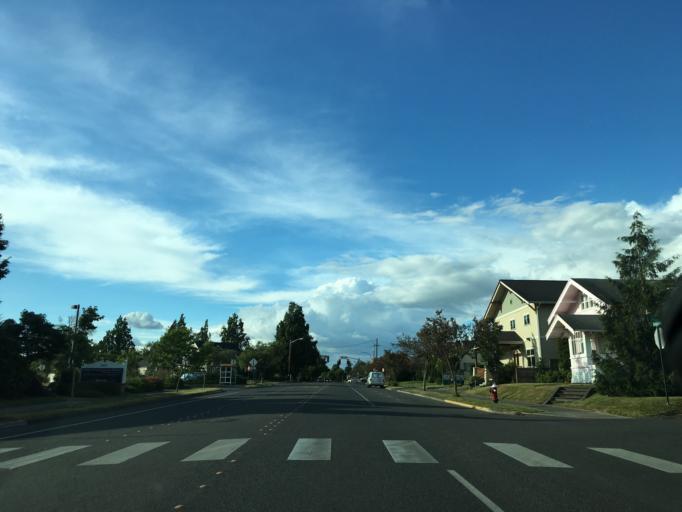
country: US
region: Washington
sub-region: Whatcom County
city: Bellingham
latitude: 48.7615
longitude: -122.4751
